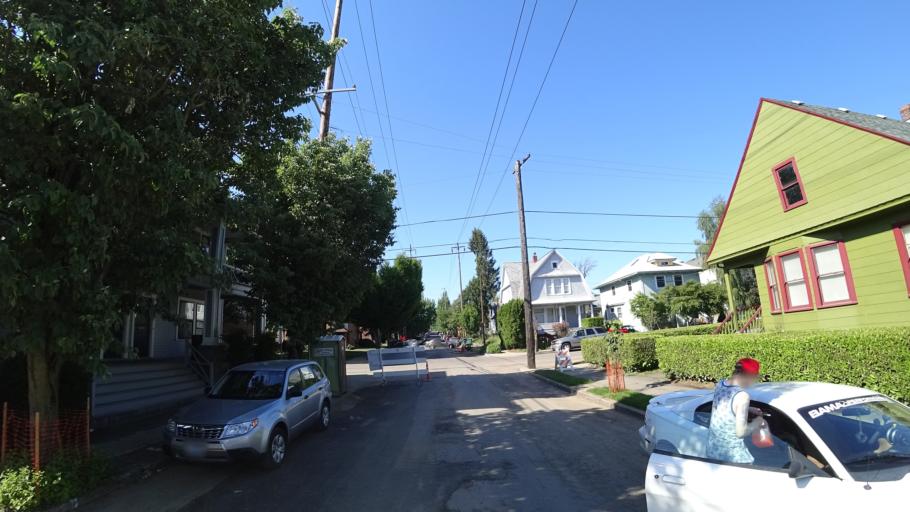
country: US
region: Oregon
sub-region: Multnomah County
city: Portland
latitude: 45.5398
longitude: -122.6642
